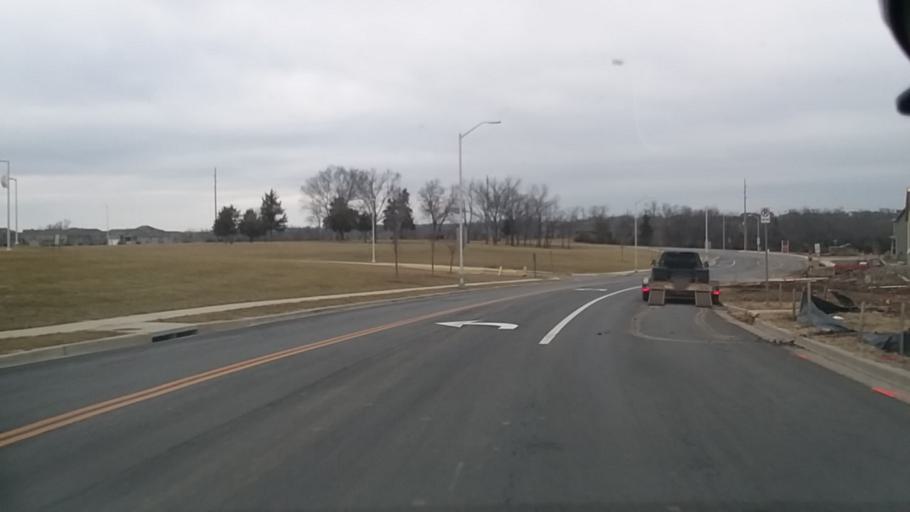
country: US
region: Kansas
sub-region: Johnson County
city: Olathe
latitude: 38.8961
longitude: -94.8670
